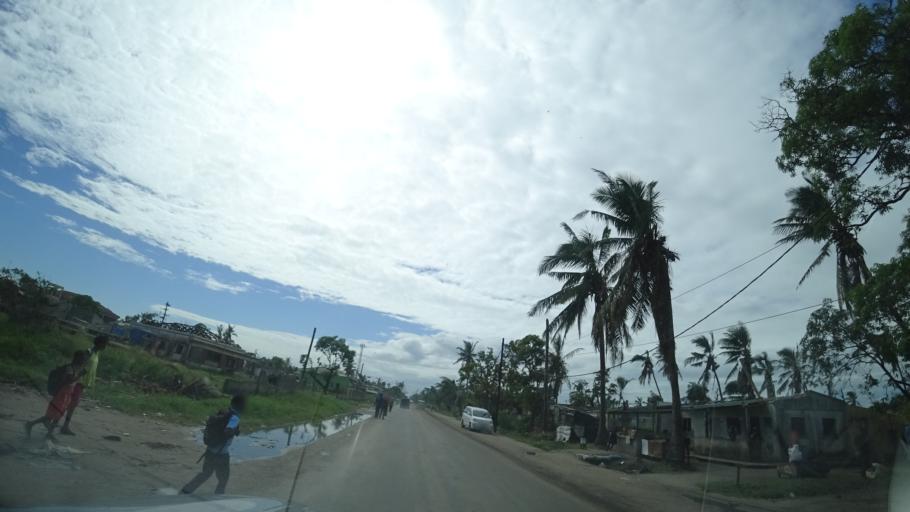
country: MZ
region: Sofala
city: Beira
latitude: -19.7735
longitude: 34.8700
